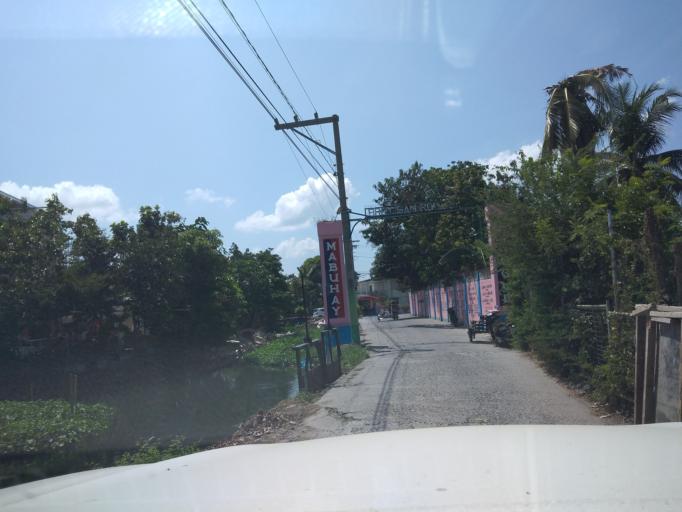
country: PH
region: Central Luzon
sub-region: Province of Pampanga
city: Lourdes
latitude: 15.0136
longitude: 120.8453
